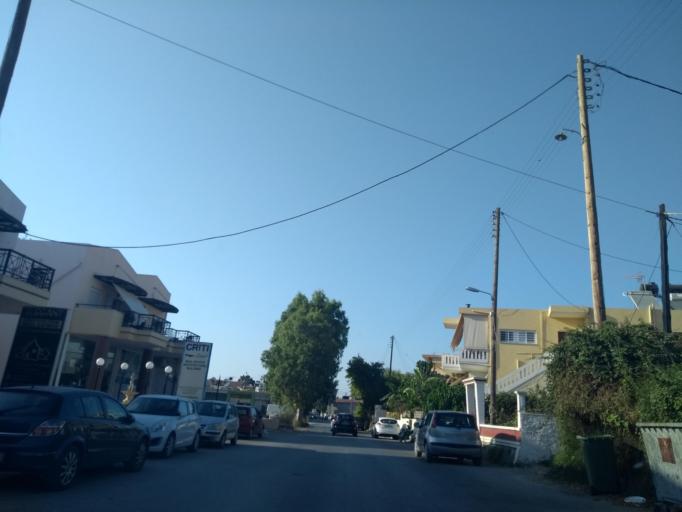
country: GR
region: Crete
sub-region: Nomos Chanias
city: Kalivai
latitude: 35.4500
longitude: 24.1743
